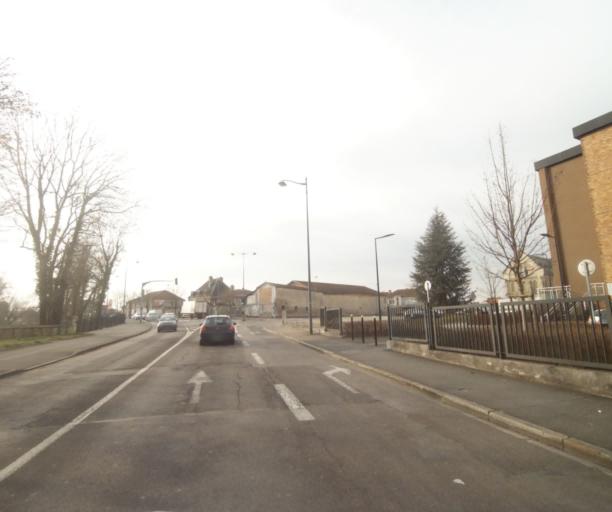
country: FR
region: Champagne-Ardenne
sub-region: Departement de la Haute-Marne
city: Saint-Dizier
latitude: 48.6327
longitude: 4.9544
